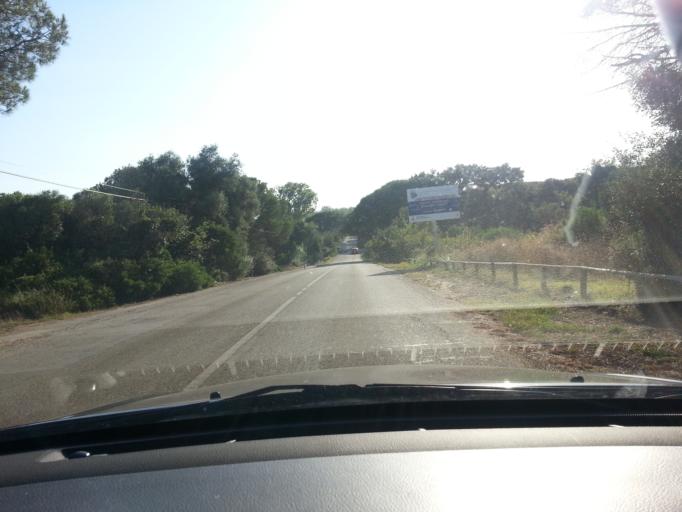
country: ES
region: Catalonia
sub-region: Provincia de Girona
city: Pals
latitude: 42.0107
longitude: 3.1845
